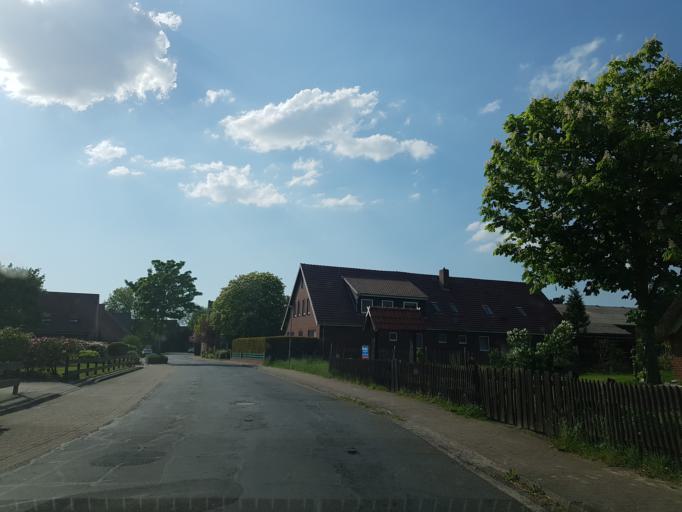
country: DE
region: Lower Saxony
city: Langen
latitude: 53.6459
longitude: 8.6033
